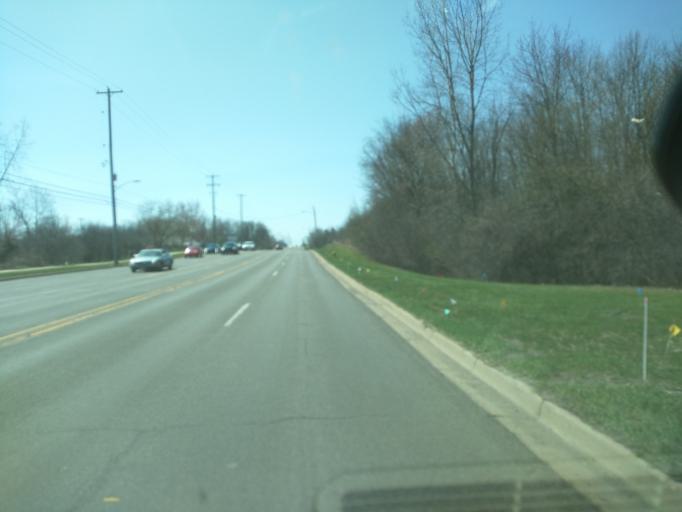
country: US
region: Michigan
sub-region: Kent County
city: East Grand Rapids
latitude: 42.9374
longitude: -85.5704
